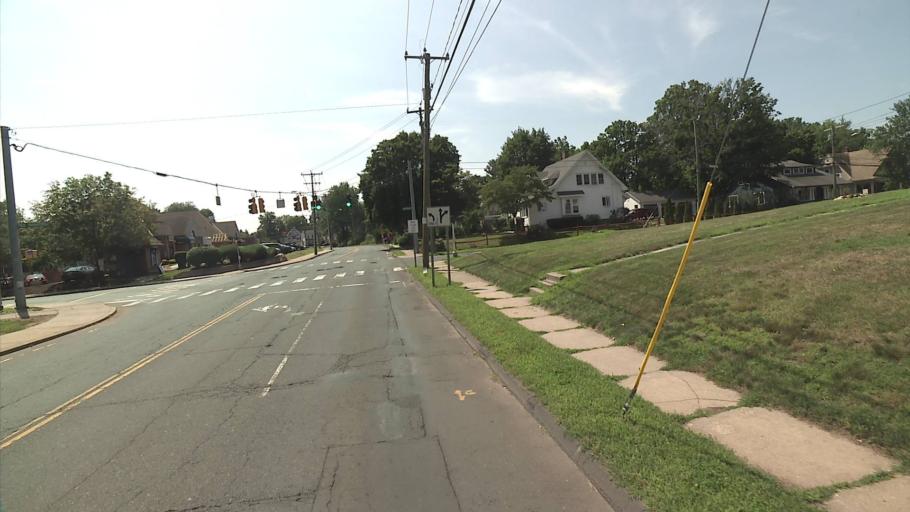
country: US
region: Connecticut
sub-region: Hartford County
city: New Britain
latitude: 41.6887
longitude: -72.7705
